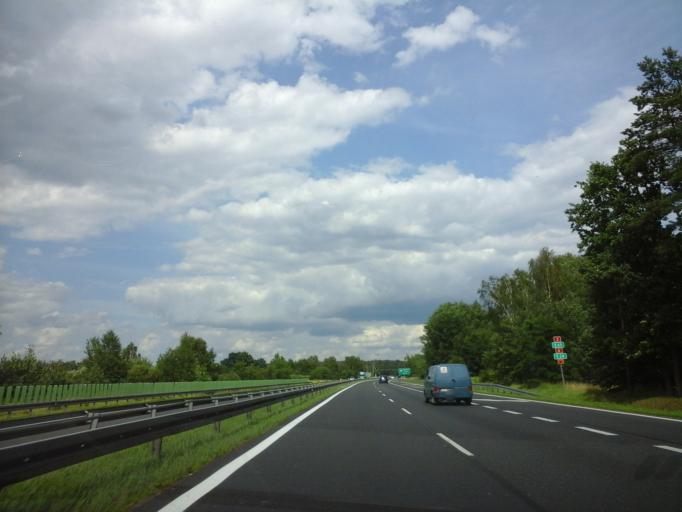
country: PL
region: West Pomeranian Voivodeship
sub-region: Powiat goleniowski
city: Goleniow
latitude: 53.5735
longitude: 14.8018
